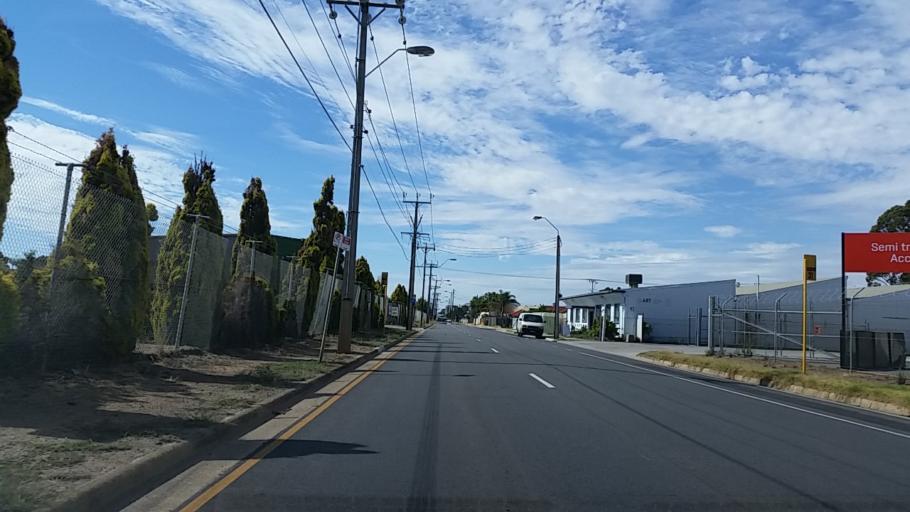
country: AU
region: South Australia
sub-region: Charles Sturt
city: Woodville North
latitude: -34.8571
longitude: 138.5383
